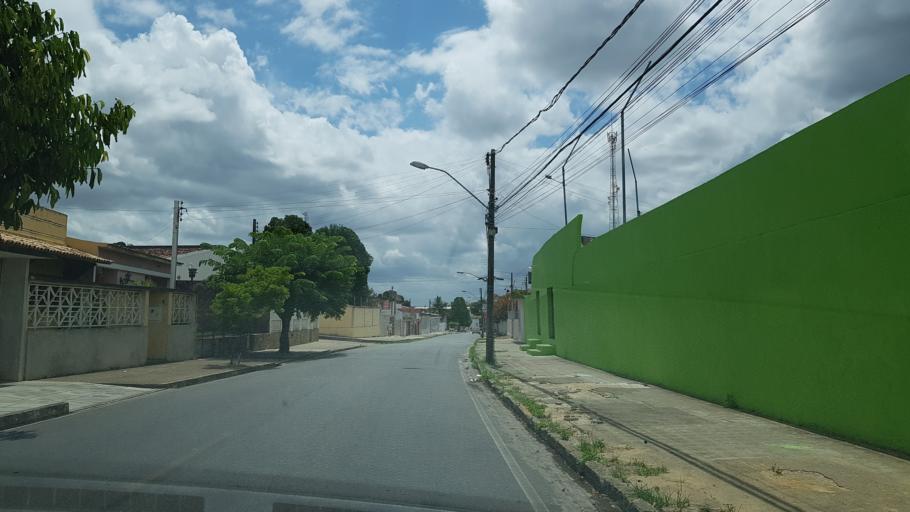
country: BR
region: Alagoas
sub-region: Penedo
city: Penedo
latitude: -10.2814
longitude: -36.5673
